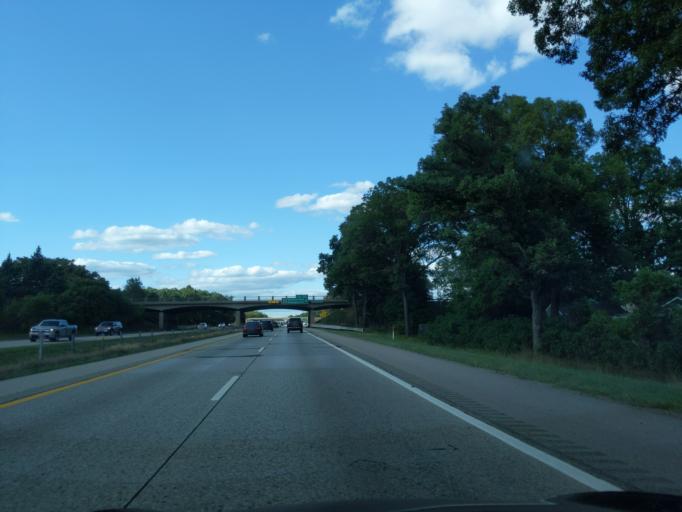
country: US
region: Michigan
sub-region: Muskegon County
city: Muskegon Heights
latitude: 43.1997
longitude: -86.2050
